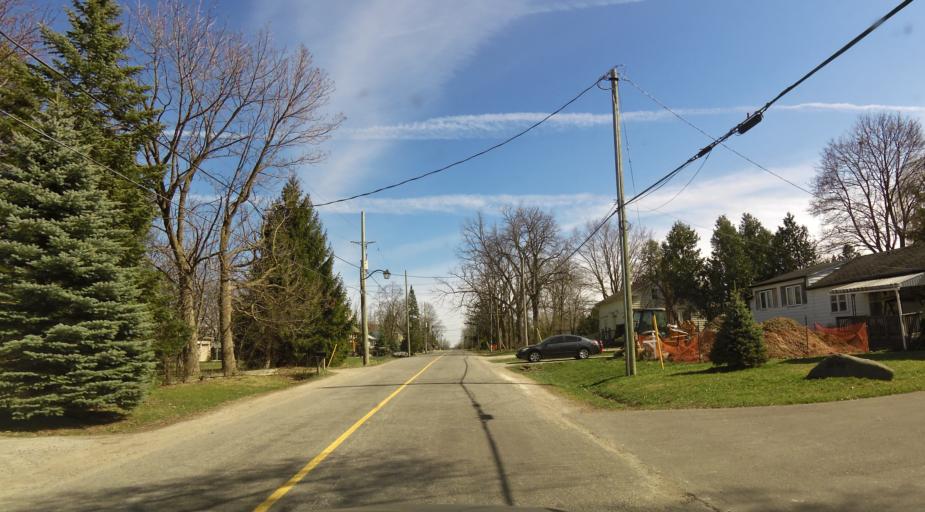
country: CA
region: Ontario
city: Brampton
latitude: 43.6299
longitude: -79.7558
